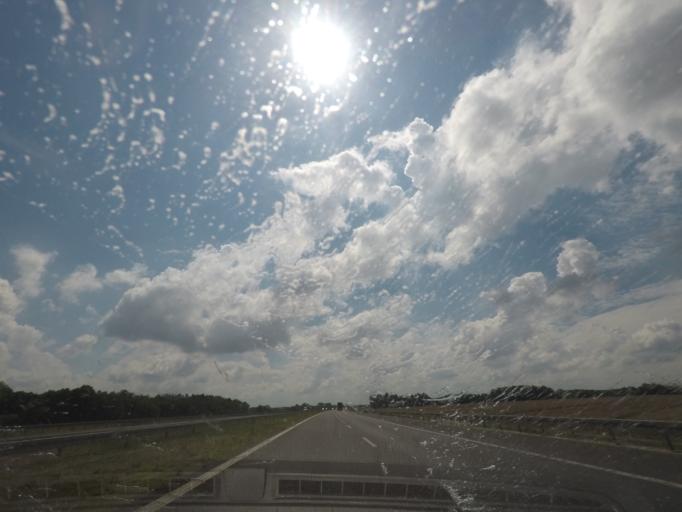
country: PL
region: Lodz Voivodeship
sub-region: Powiat zgierski
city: Strykow
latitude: 51.9477
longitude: 19.6064
